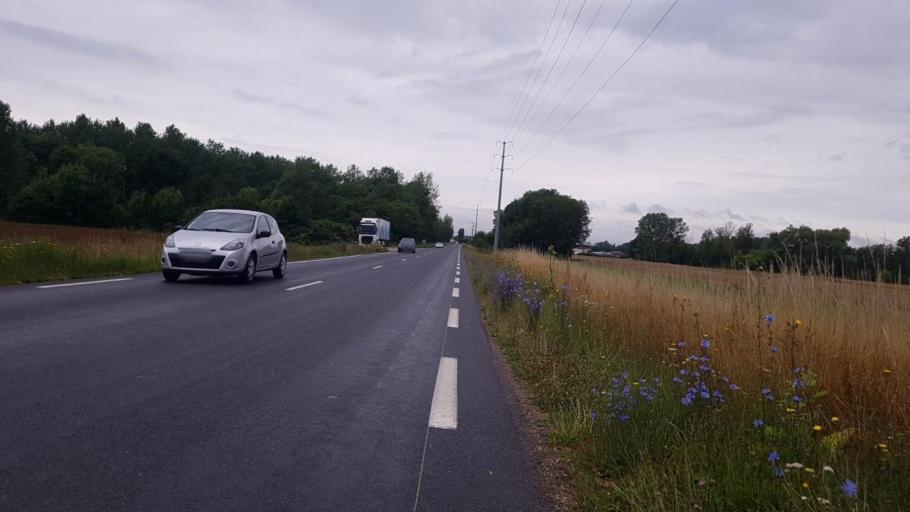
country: FR
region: Champagne-Ardenne
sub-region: Departement de la Marne
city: Vitry-le-Francois
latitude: 48.7409
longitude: 4.6487
